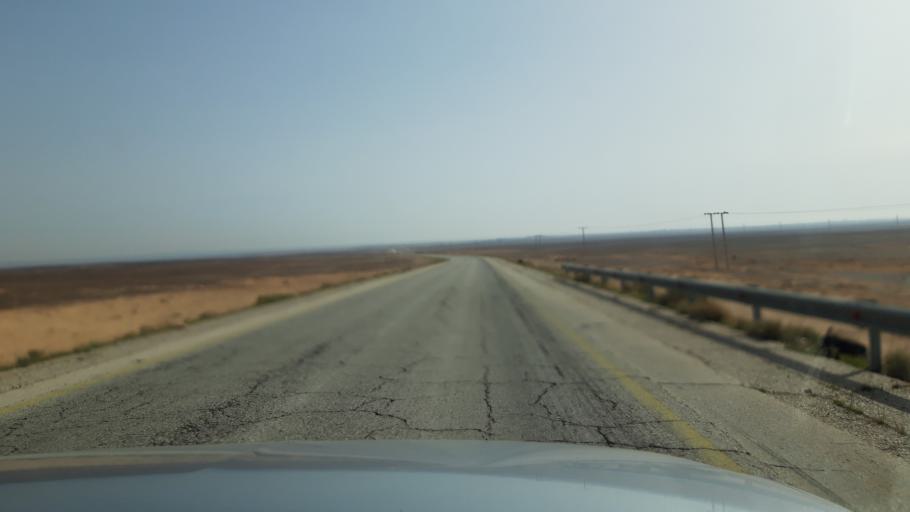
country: JO
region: Amman
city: Al Azraq ash Shamali
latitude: 31.8536
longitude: 36.6828
